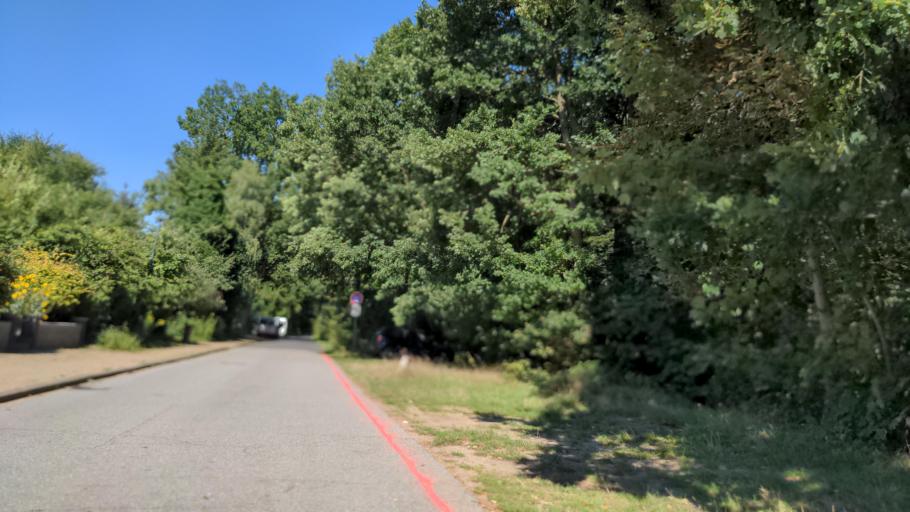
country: DE
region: Schleswig-Holstein
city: Bliestorf
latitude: 53.7723
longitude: 10.6005
